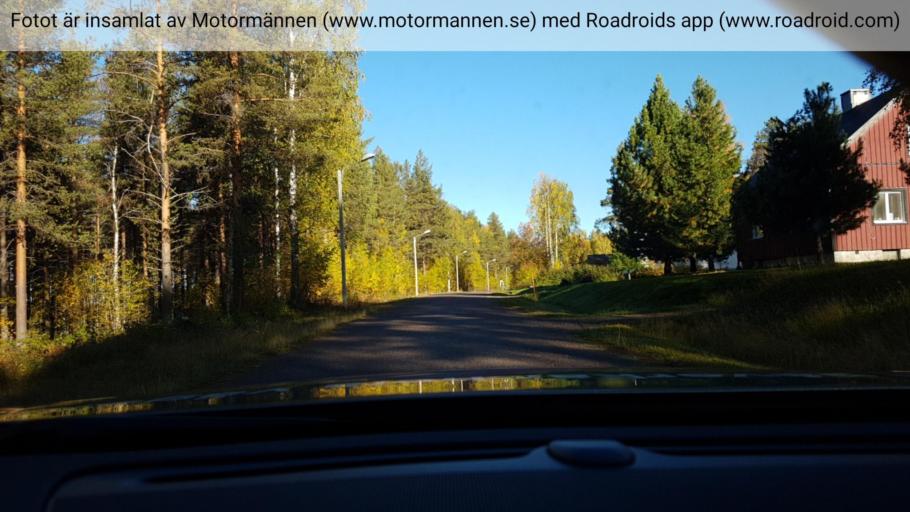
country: SE
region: Norrbotten
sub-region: Alvsbyns Kommun
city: AElvsbyn
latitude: 66.2736
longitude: 21.1208
